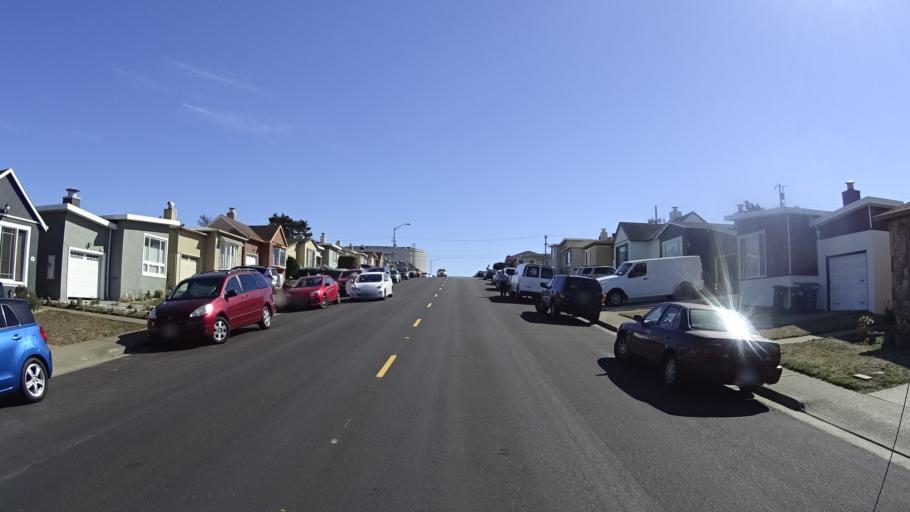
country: US
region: California
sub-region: San Mateo County
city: Broadmoor
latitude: 37.6726
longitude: -122.4892
